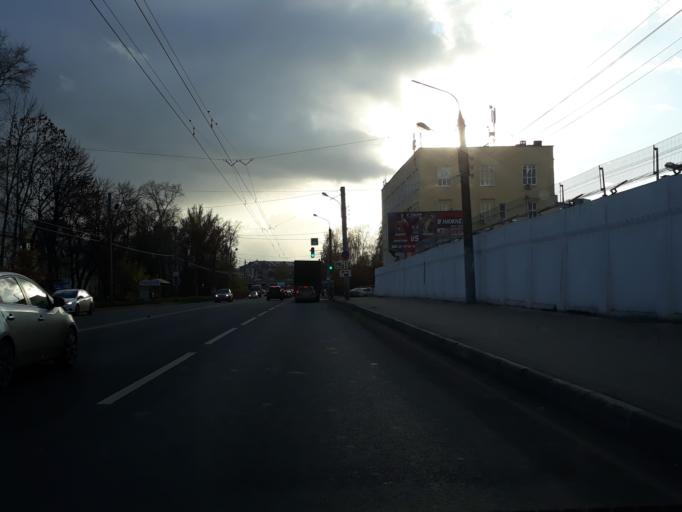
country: RU
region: Nizjnij Novgorod
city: Nizhniy Novgorod
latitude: 56.3175
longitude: 43.9023
